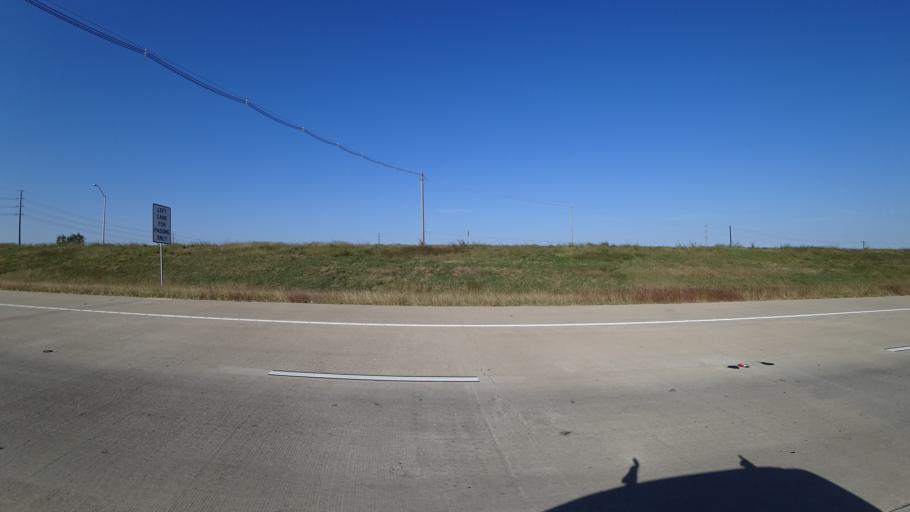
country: US
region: Texas
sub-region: Travis County
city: Garfield
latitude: 30.1615
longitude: -97.6537
